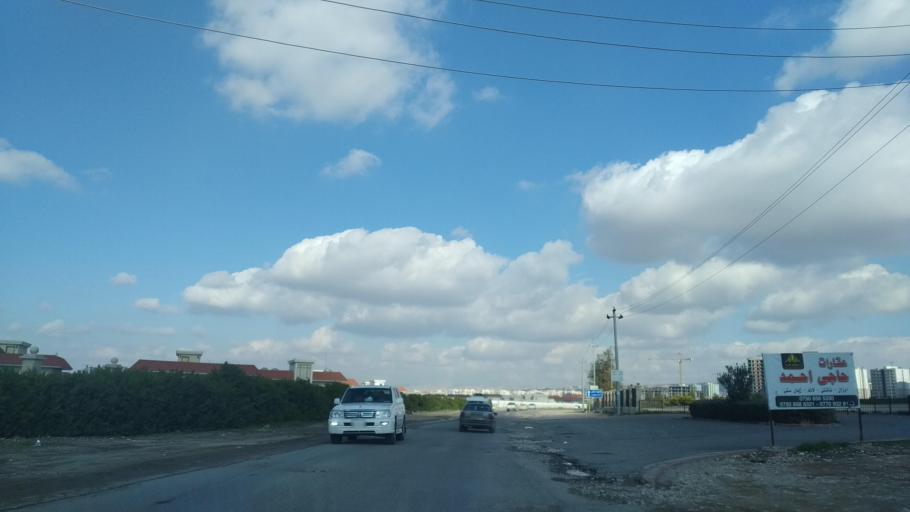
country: IQ
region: Arbil
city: Erbil
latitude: 36.2091
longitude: 44.1340
